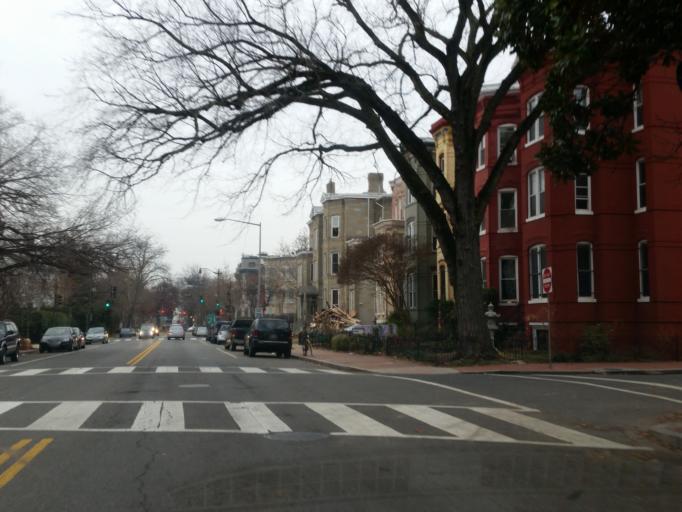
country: US
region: Washington, D.C.
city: Washington, D.C.
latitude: 38.9121
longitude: -77.0296
